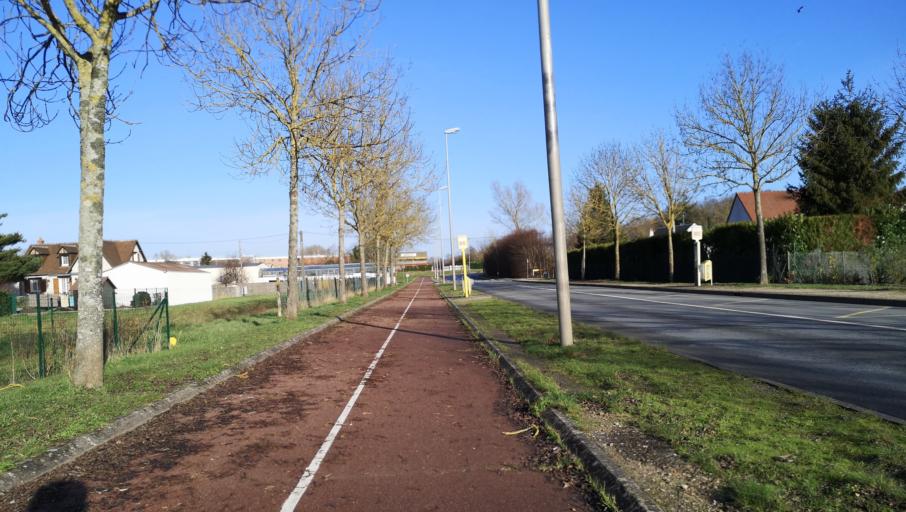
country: FR
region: Centre
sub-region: Departement du Loiret
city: Saint-Jean-le-Blanc
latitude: 47.8909
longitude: 1.9305
